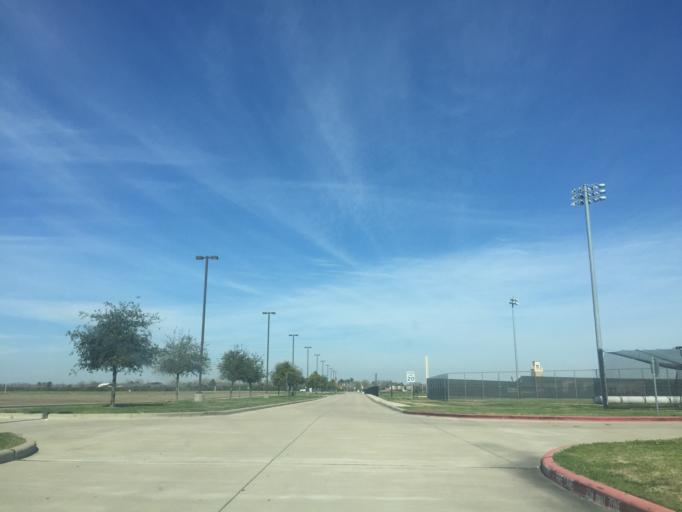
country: US
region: Texas
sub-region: Galveston County
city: Kemah
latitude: 29.5110
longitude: -95.0255
